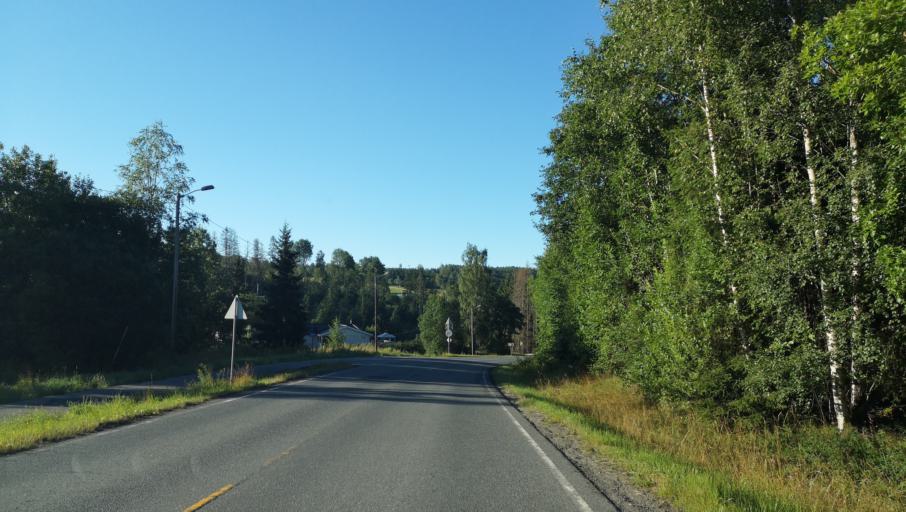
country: NO
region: Ostfold
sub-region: Hobol
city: Tomter
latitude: 59.6568
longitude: 11.0014
